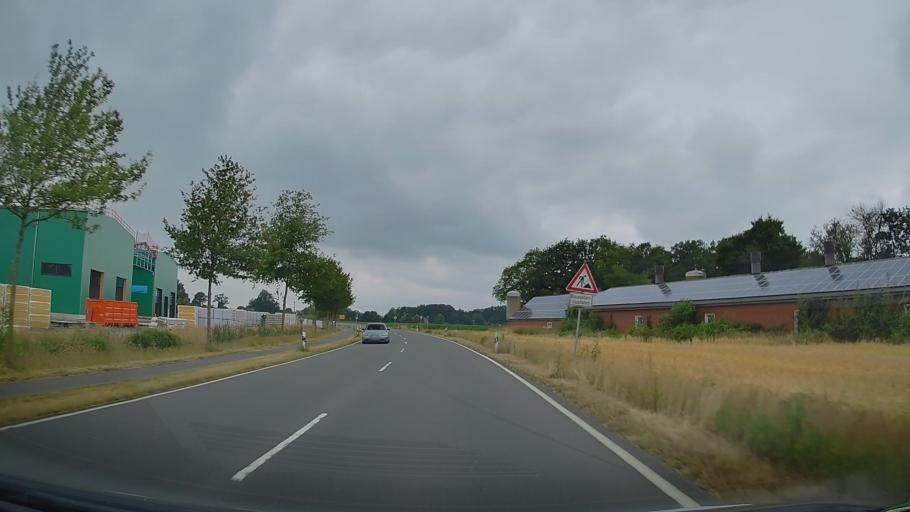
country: DE
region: Lower Saxony
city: Dinklage
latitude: 52.6779
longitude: 8.1347
